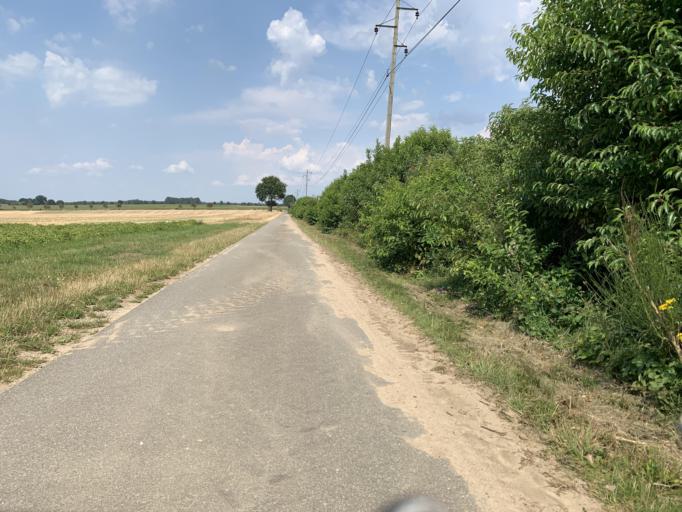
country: DE
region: Lower Saxony
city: Thomasburg
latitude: 53.2123
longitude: 10.6369
